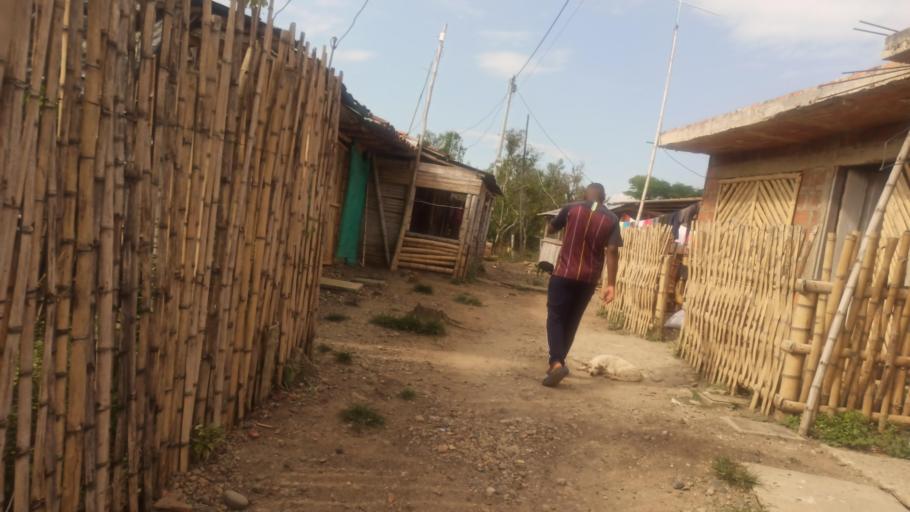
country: CO
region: Valle del Cauca
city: Jamundi
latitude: 3.1271
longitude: -76.5580
